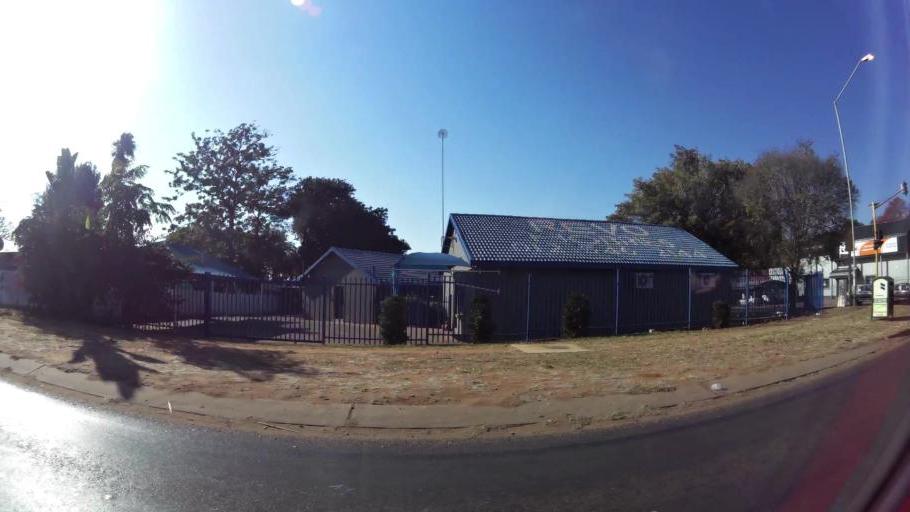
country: ZA
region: Gauteng
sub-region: City of Tshwane Metropolitan Municipality
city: Pretoria
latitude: -25.6767
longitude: 28.1652
